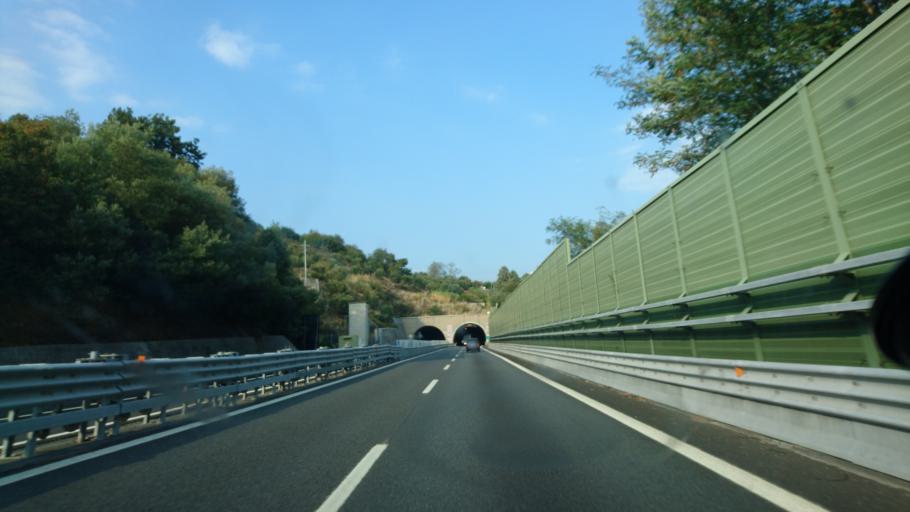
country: IT
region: Liguria
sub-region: Provincia di Savona
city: Savona
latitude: 44.3121
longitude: 8.4678
